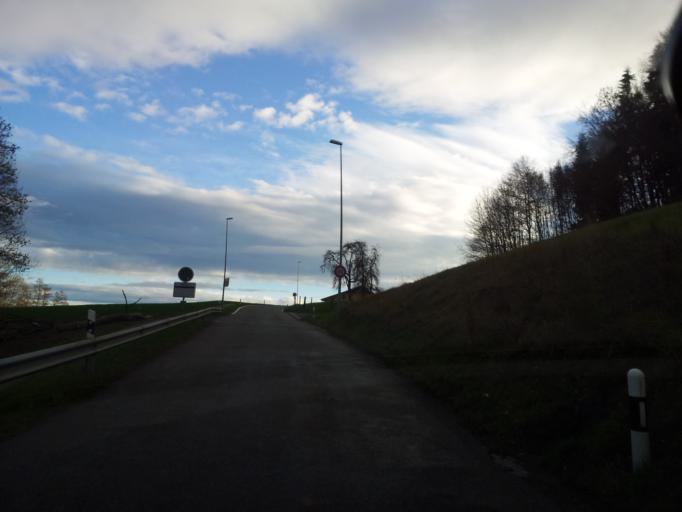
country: CH
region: Aargau
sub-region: Bezirk Bremgarten
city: Rudolfstetten
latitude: 47.3852
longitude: 8.3862
